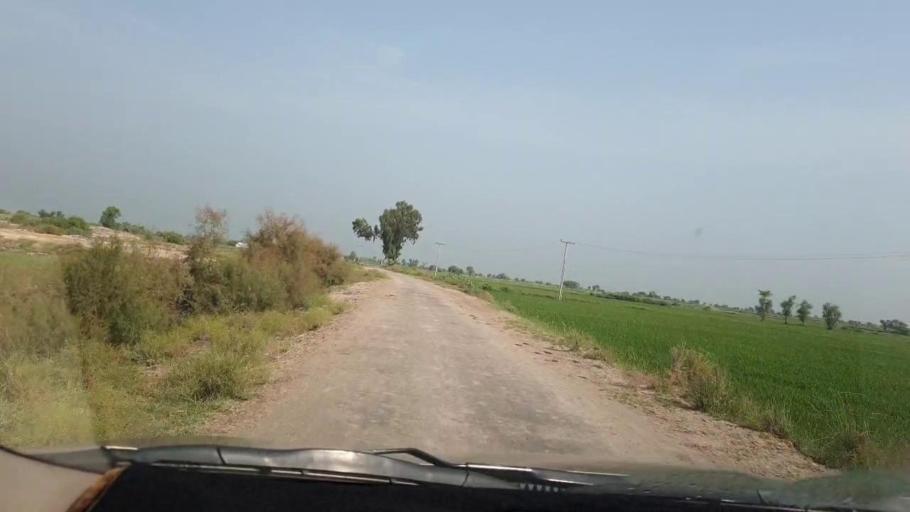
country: PK
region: Sindh
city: Goth Garelo
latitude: 27.4601
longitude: 68.0529
